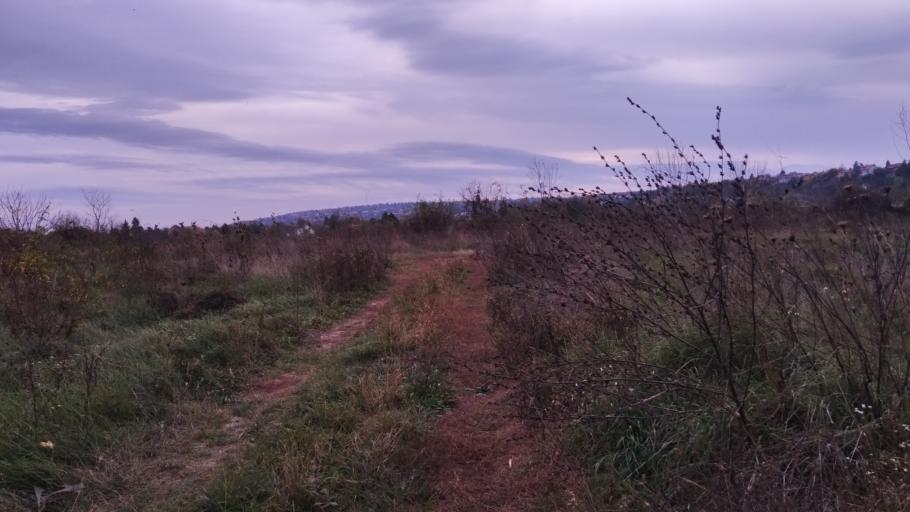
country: HU
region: Pest
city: Pomaz
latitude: 47.6359
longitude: 19.0459
